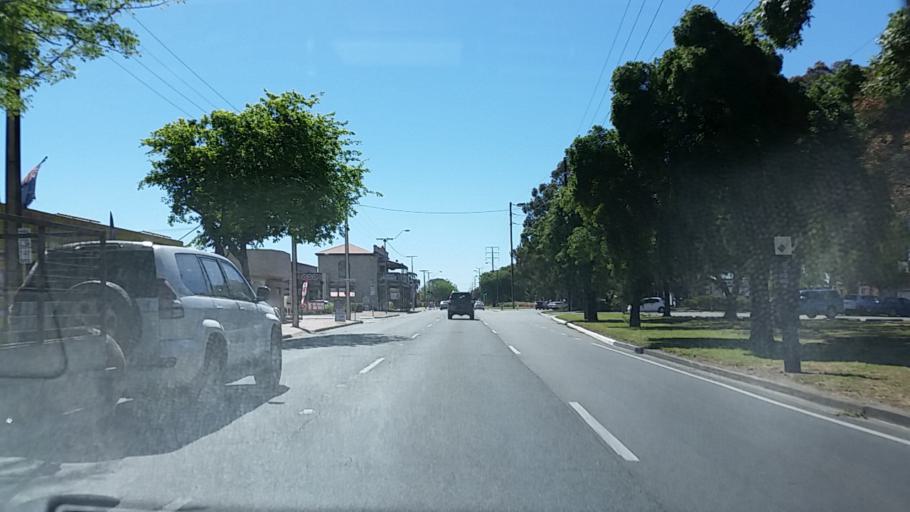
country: AU
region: South Australia
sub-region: Charles Sturt
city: Woodville
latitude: -34.8906
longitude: 138.5496
